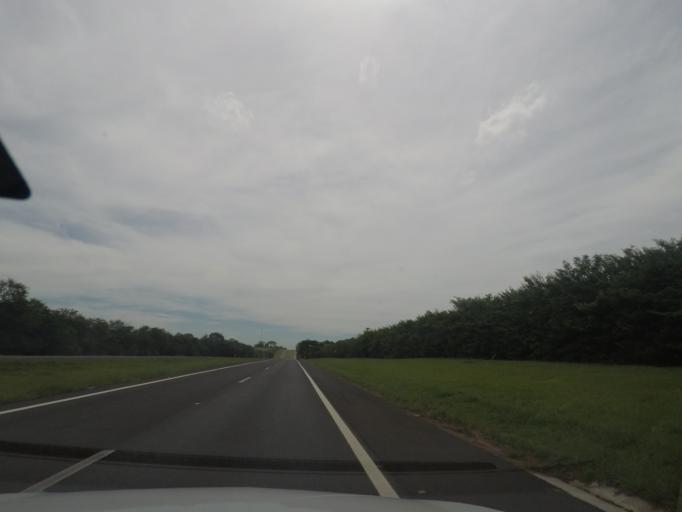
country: BR
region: Sao Paulo
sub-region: Bebedouro
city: Bebedouro
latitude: -20.9764
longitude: -48.4382
